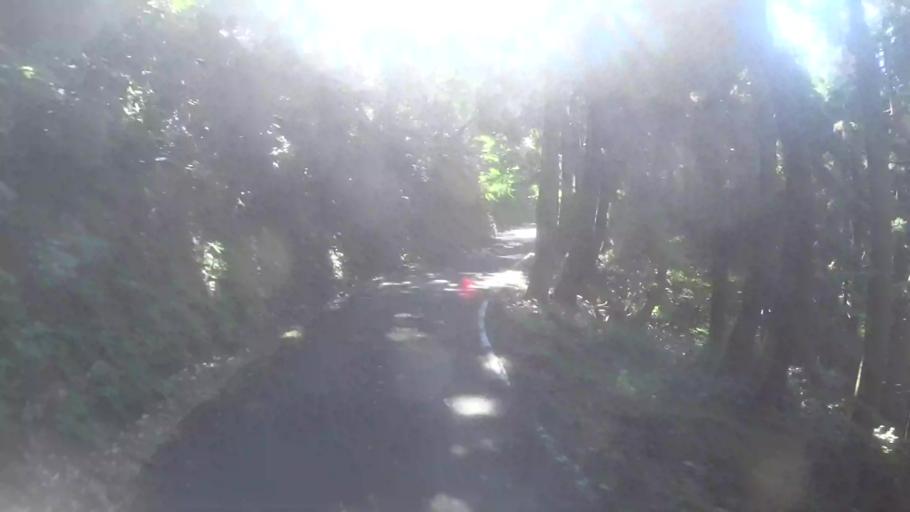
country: JP
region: Kyoto
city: Miyazu
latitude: 35.6640
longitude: 135.1317
